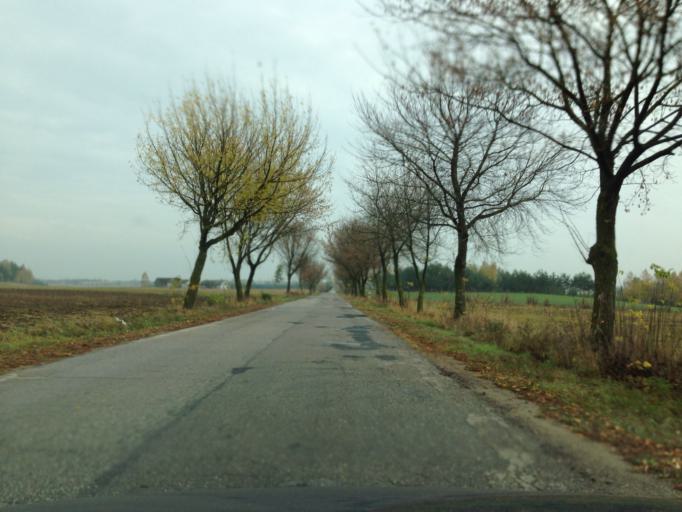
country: PL
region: Kujawsko-Pomorskie
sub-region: Powiat brodnicki
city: Gorzno
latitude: 53.1692
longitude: 19.6189
